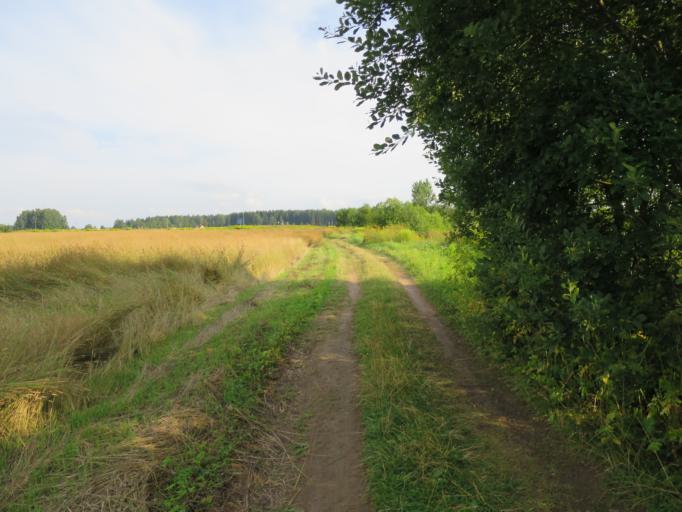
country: LV
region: Priekuli
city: Priekuli
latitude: 57.3170
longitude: 25.3188
